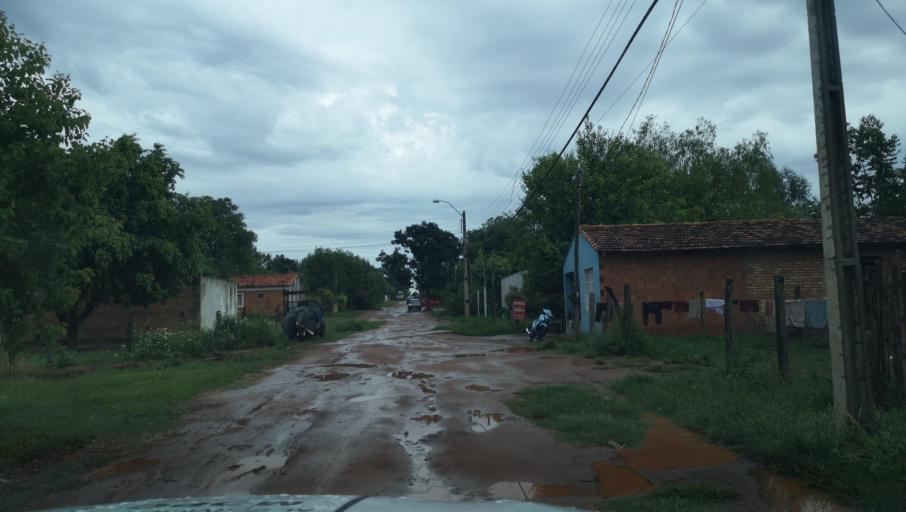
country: PY
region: Misiones
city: Santa Maria
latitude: -26.8997
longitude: -57.0337
